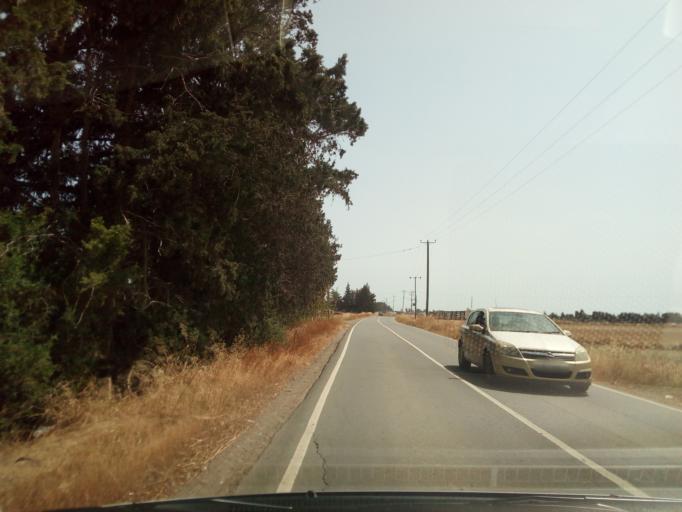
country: CY
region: Larnaka
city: Meneou
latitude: 34.8530
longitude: 33.5954
